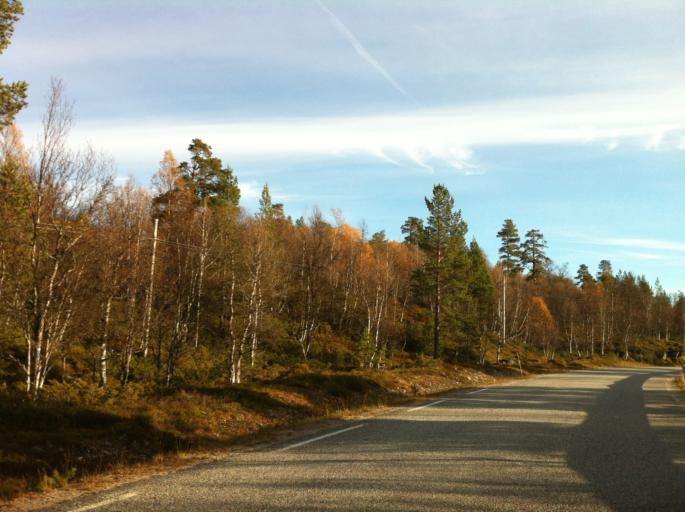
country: NO
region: Hedmark
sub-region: Engerdal
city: Engerdal
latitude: 62.1130
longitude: 12.0177
